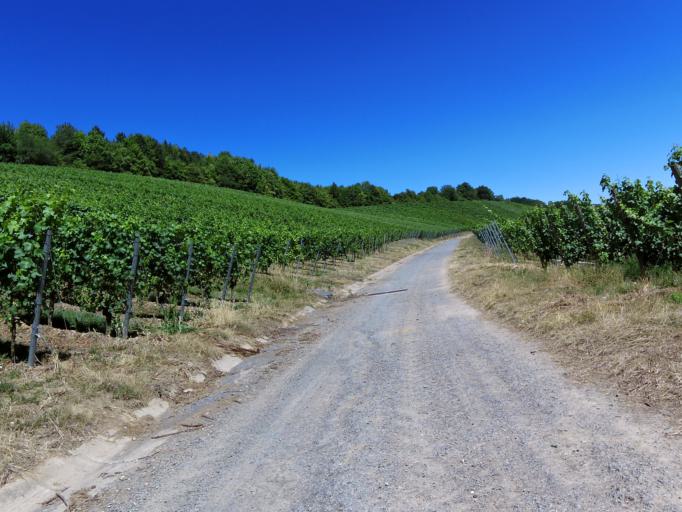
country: DE
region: Bavaria
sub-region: Regierungsbezirk Unterfranken
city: Gerbrunn
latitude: 49.7581
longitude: 10.0022
